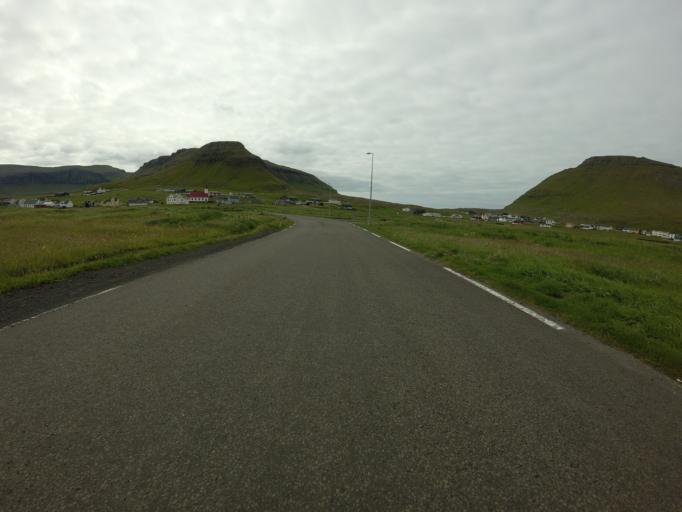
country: FO
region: Suduroy
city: Tvoroyri
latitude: 61.6007
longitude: -6.9531
